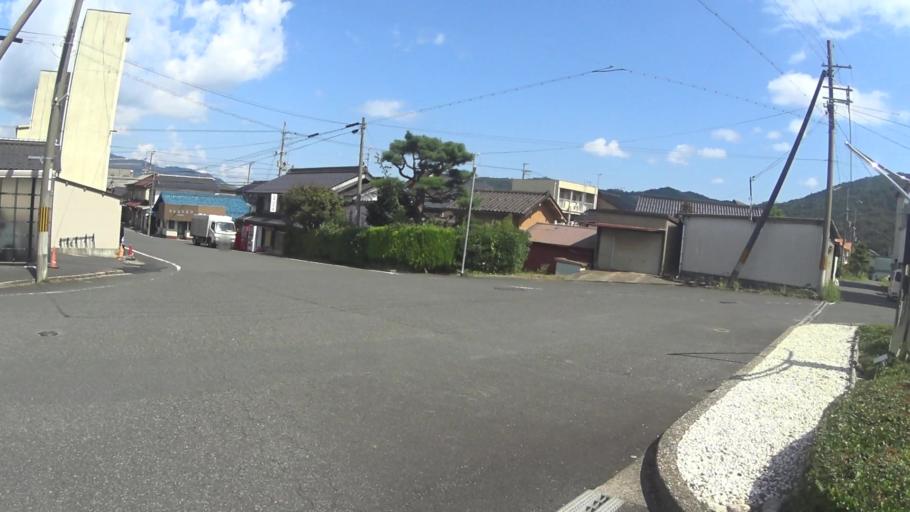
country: JP
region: Kyoto
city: Miyazu
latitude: 35.5506
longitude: 135.1512
